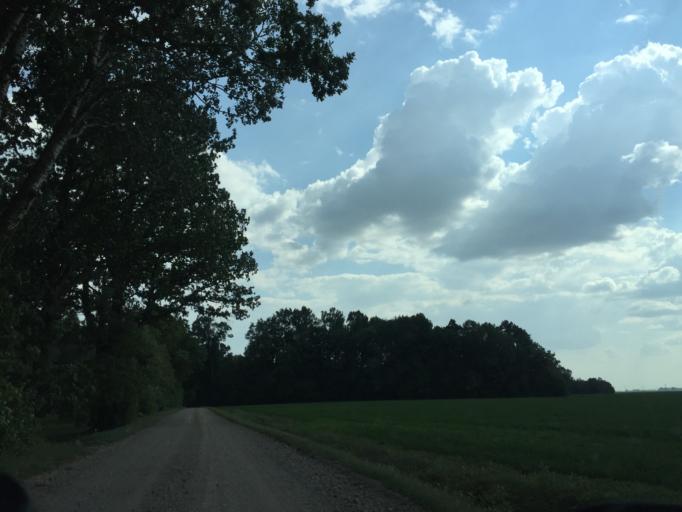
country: LV
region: Jelgava
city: Jelgava
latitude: 56.5078
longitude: 23.7549
